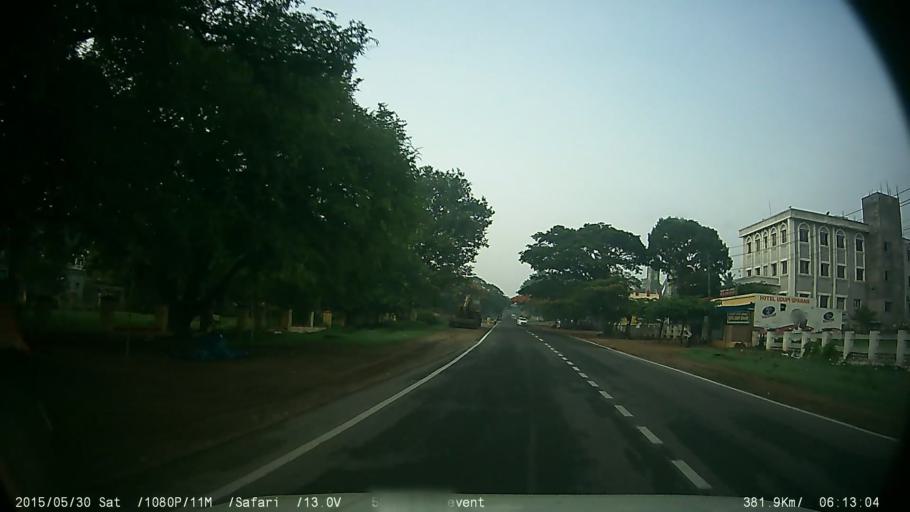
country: IN
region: Karnataka
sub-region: Mysore
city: Mysore
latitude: 12.3378
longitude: 76.6578
